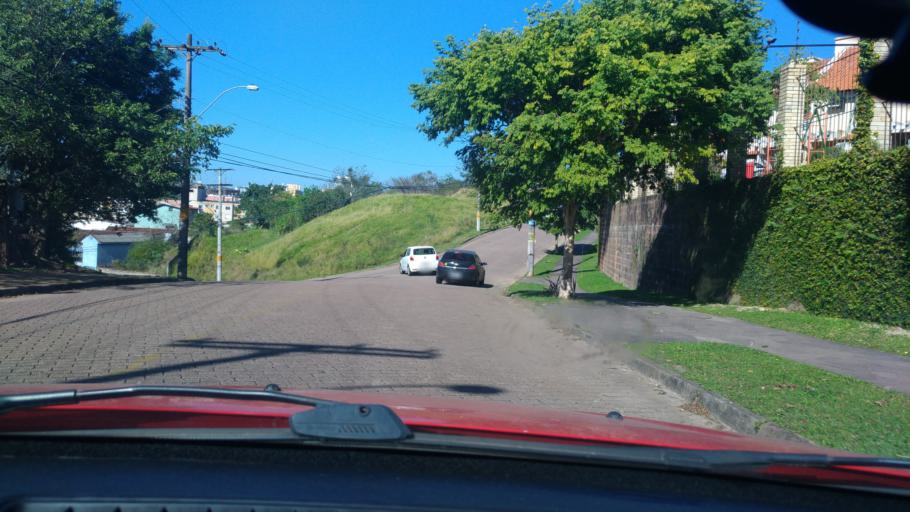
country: BR
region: Rio Grande do Sul
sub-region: Porto Alegre
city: Porto Alegre
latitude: -30.0354
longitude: -51.1457
